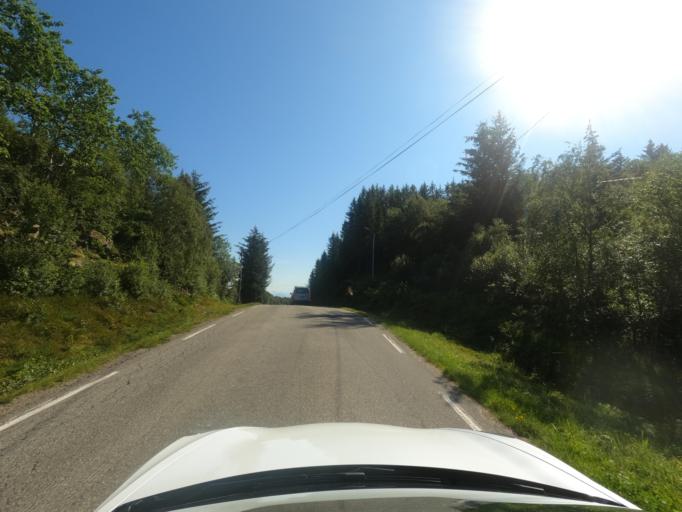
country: NO
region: Nordland
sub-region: Hadsel
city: Stokmarknes
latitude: 68.3033
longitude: 15.0355
